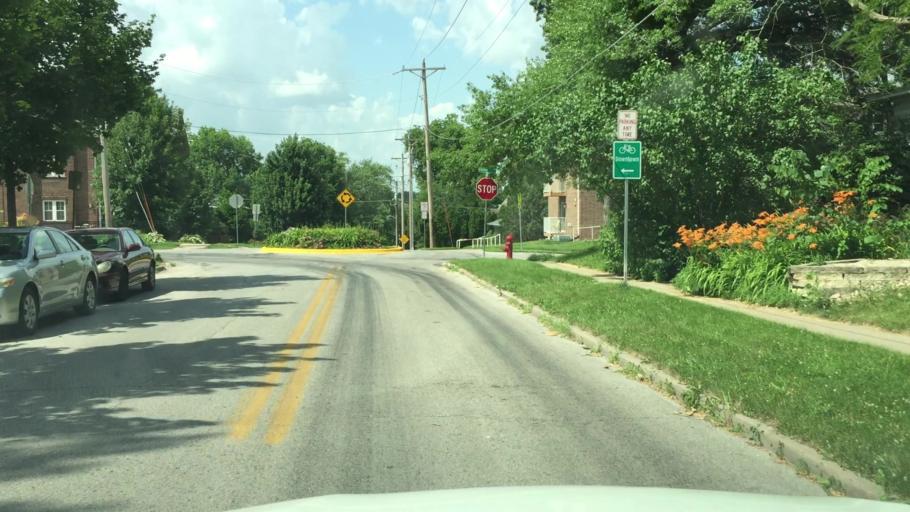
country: US
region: Iowa
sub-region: Johnson County
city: Iowa City
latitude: 41.6585
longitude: -91.5212
